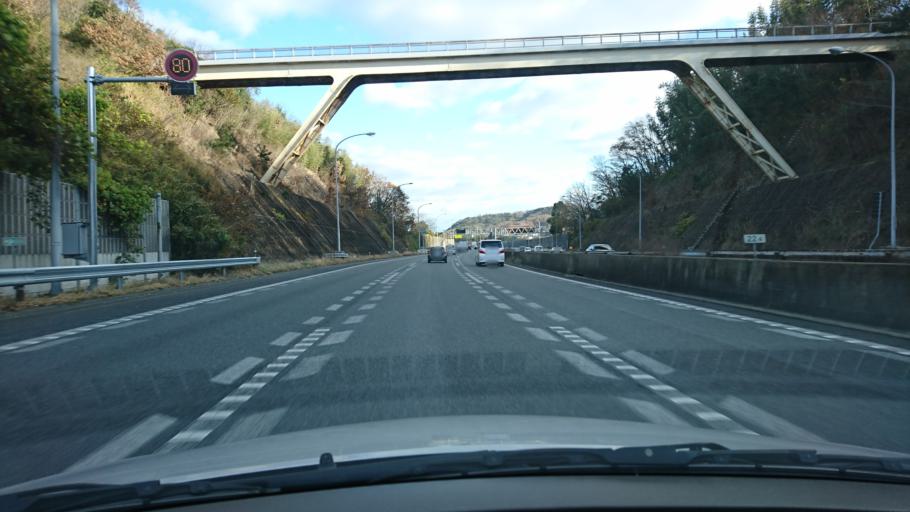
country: JP
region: Hyogo
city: Takarazuka
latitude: 34.8240
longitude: 135.3138
